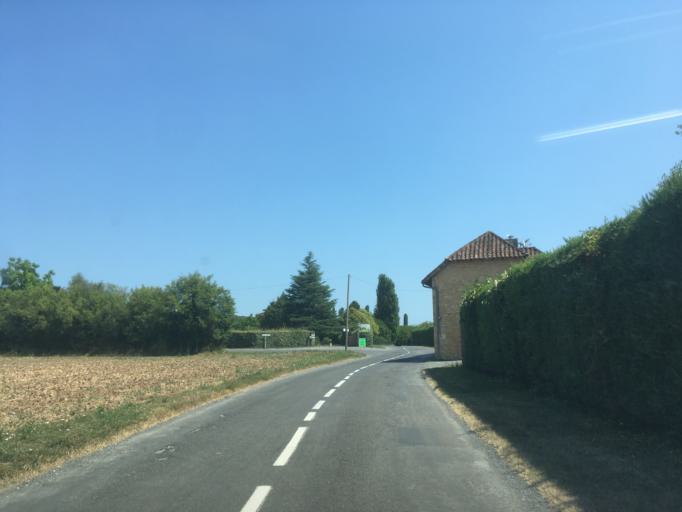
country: FR
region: Aquitaine
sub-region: Departement de la Dordogne
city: Montignac
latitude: 45.0706
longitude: 1.1714
